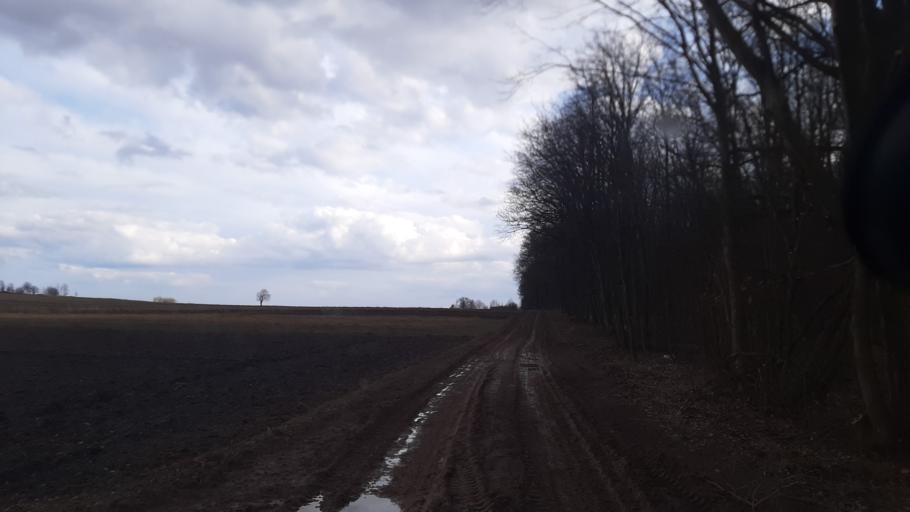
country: PL
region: Lublin Voivodeship
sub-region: Powiat lubelski
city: Jastkow
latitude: 51.3761
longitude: 22.4132
